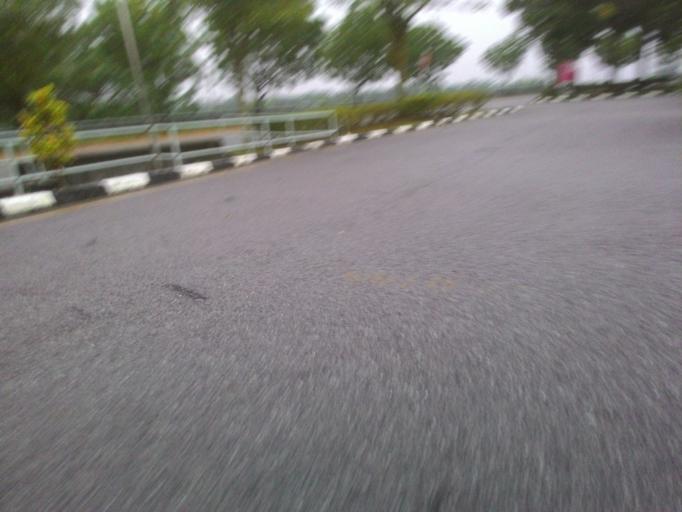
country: MY
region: Kedah
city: Kulim
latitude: 5.3825
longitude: 100.5767
